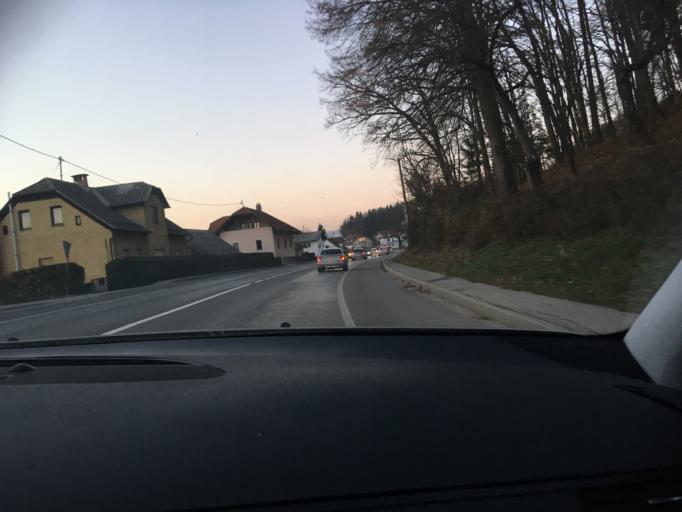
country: SI
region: Skofljica
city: Skofljica
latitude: 45.9881
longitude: 14.5676
